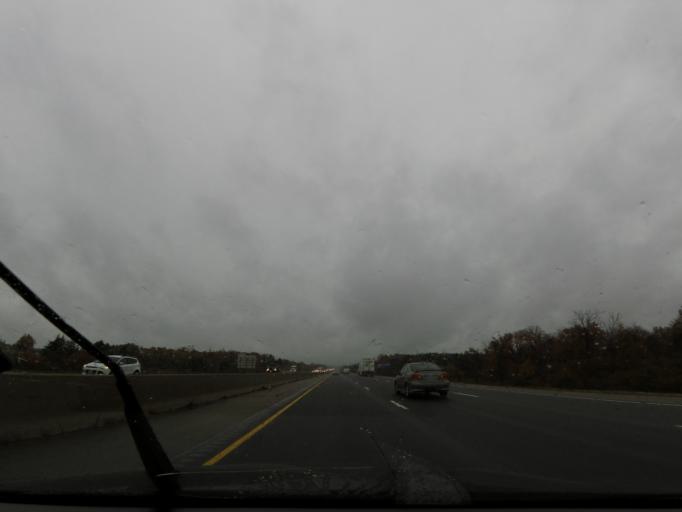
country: CA
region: Ontario
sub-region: Wellington County
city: Guelph
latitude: 43.4429
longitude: -80.2026
